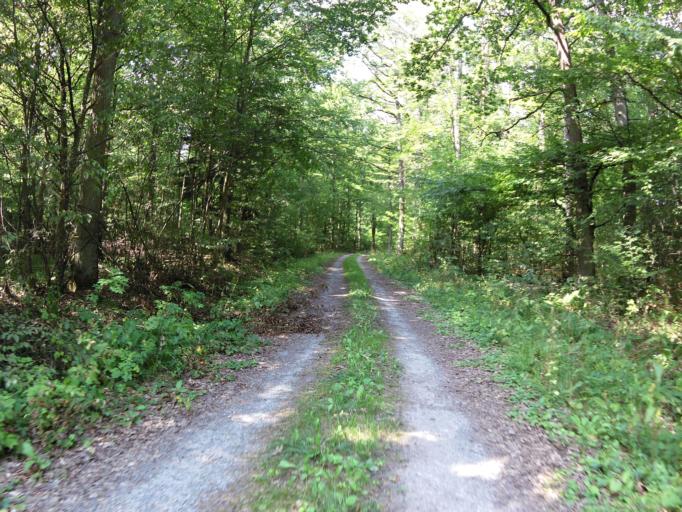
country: DE
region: Bavaria
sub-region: Regierungsbezirk Unterfranken
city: Kleinrinderfeld
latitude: 49.7048
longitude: 9.8232
